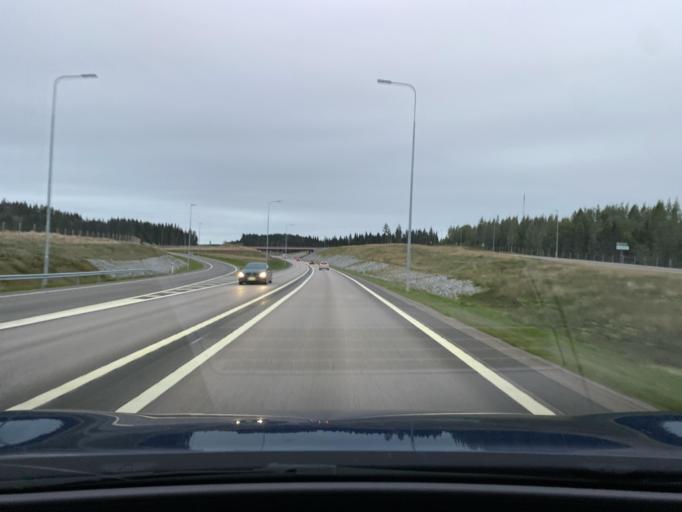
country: FI
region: Paijanne Tavastia
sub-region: Lahti
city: Hollola
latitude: 60.9635
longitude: 25.5233
